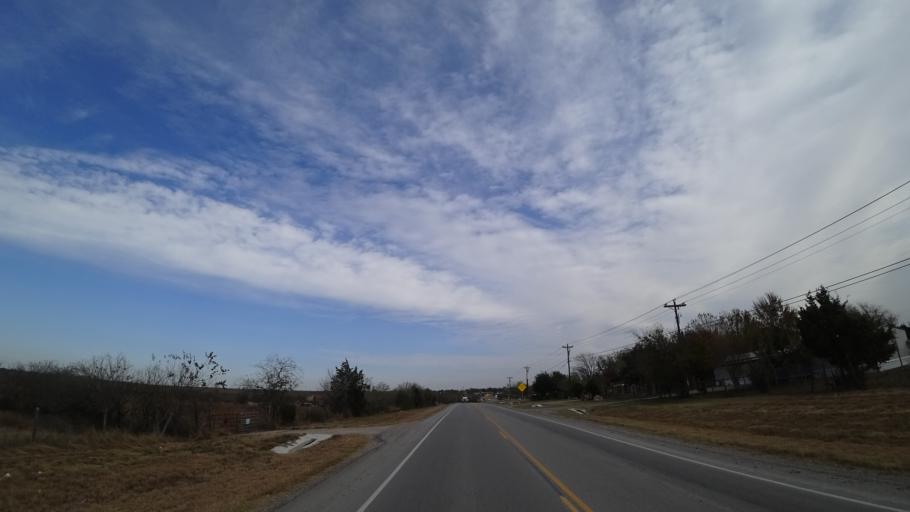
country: US
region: Texas
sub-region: Travis County
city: Onion Creek
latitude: 30.1417
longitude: -97.6765
